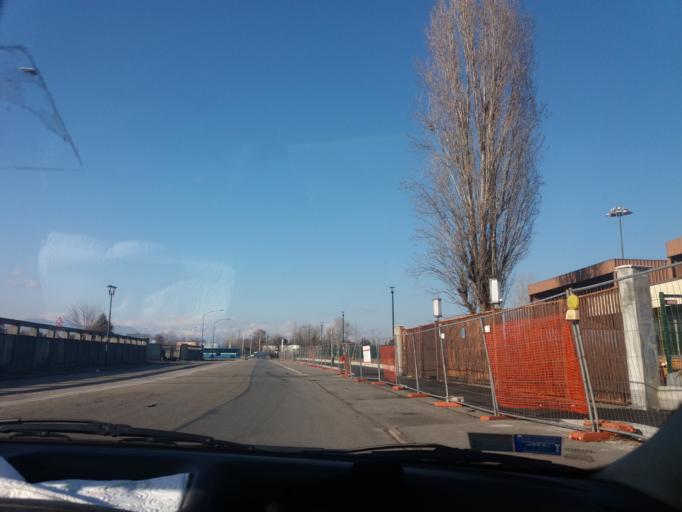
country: IT
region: Piedmont
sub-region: Provincia di Torino
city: Fornaci
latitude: 45.0285
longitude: 7.6090
